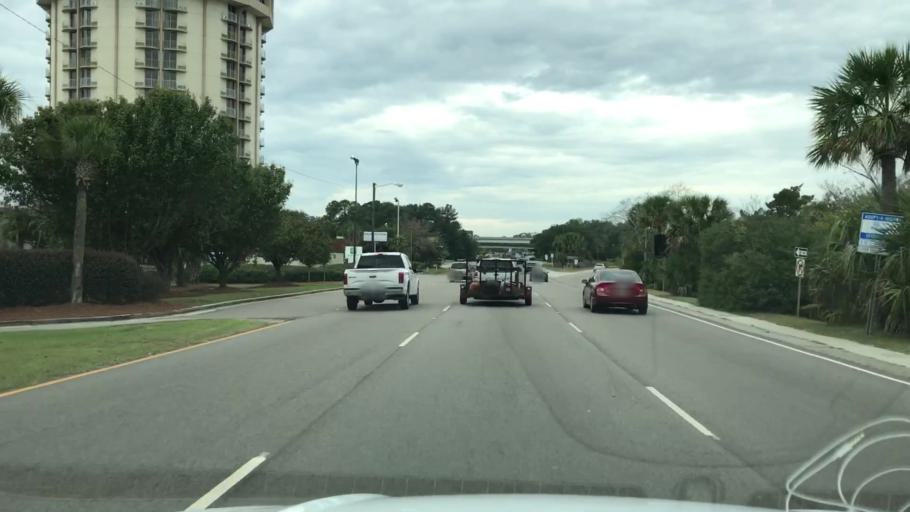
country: US
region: South Carolina
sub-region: Charleston County
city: Charleston
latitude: 32.7820
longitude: -79.9643
